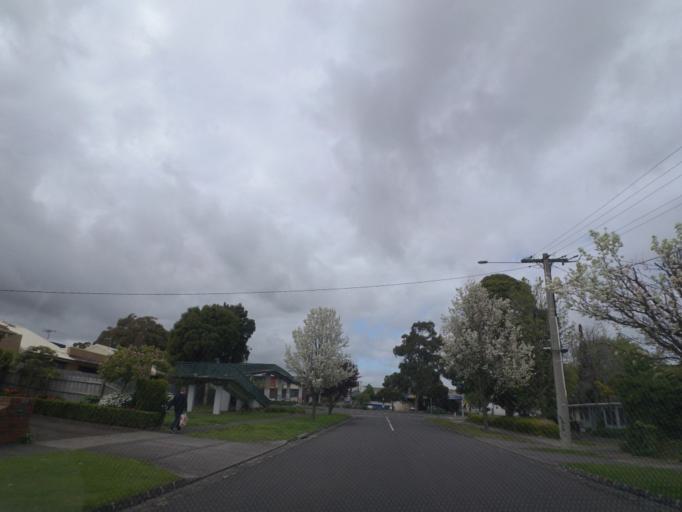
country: AU
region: Victoria
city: Mitcham
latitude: -37.8162
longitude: 145.1895
